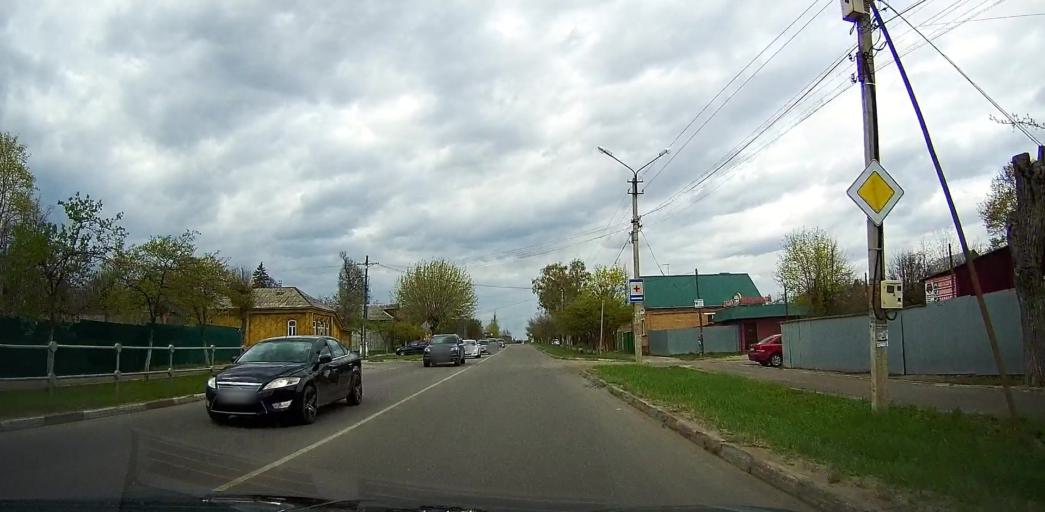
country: RU
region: Moskovskaya
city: Pavlovskiy Posad
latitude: 55.7869
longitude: 38.6474
